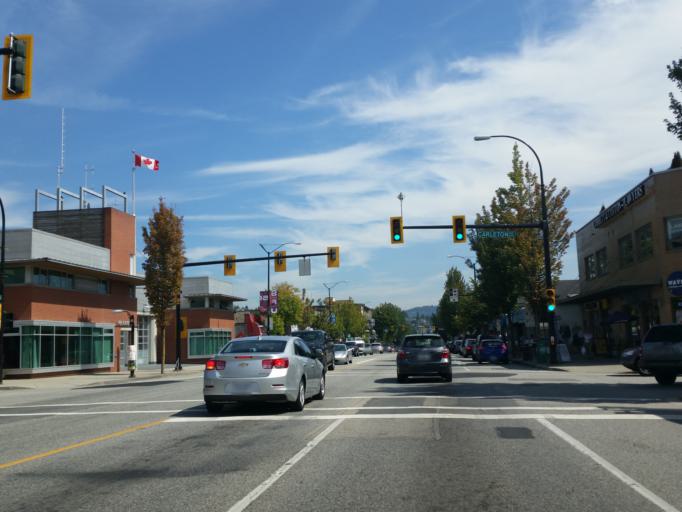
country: CA
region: British Columbia
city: Burnaby
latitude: 49.2810
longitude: -123.0118
